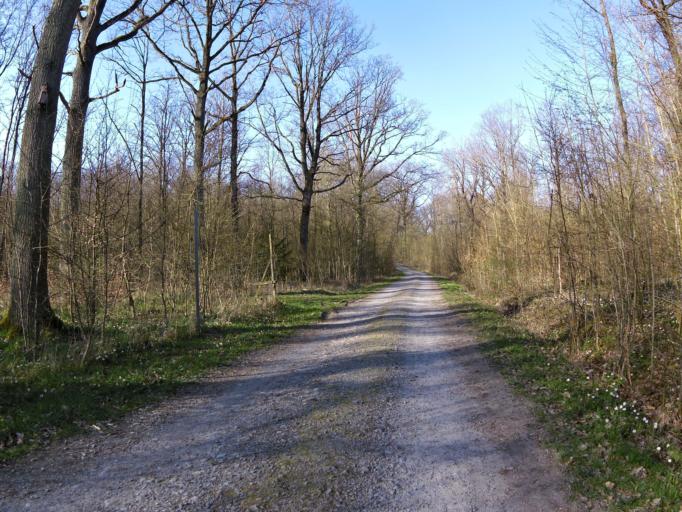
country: DE
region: Bavaria
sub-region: Regierungsbezirk Unterfranken
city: Kurnach
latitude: 49.8287
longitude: 10.0579
